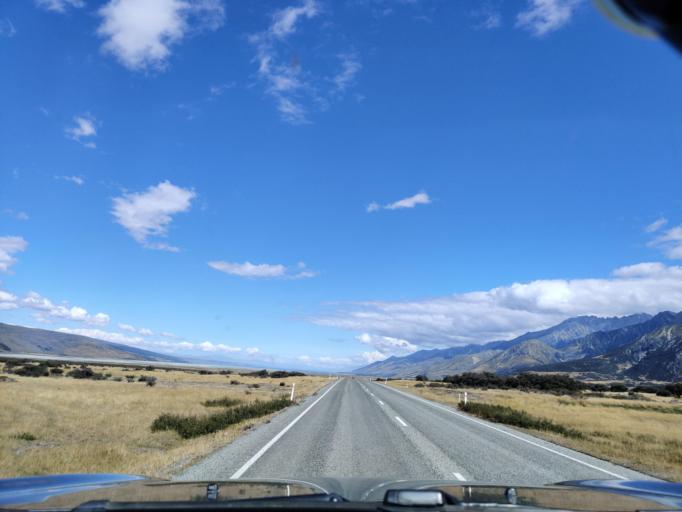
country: NZ
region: Canterbury
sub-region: Timaru District
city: Pleasant Point
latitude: -43.7732
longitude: 170.1232
